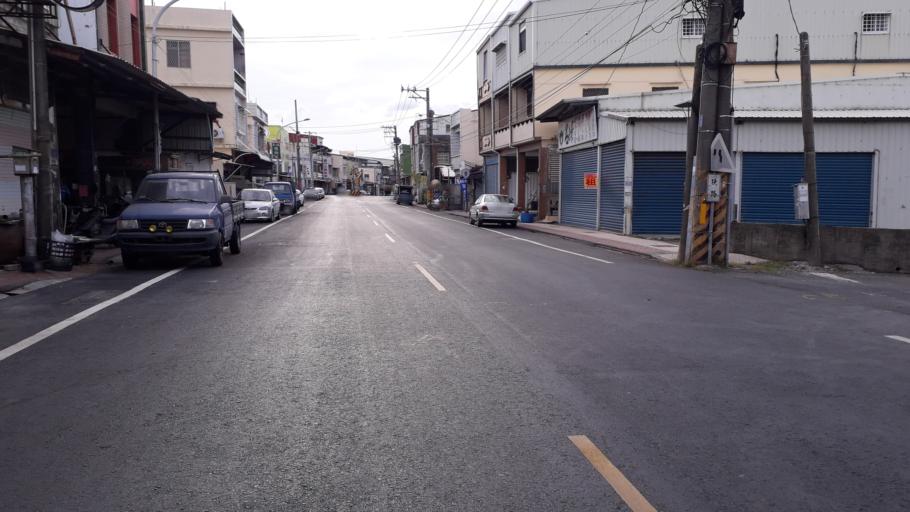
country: TW
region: Taiwan
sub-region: Pingtung
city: Pingtung
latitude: 22.3655
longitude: 120.6010
